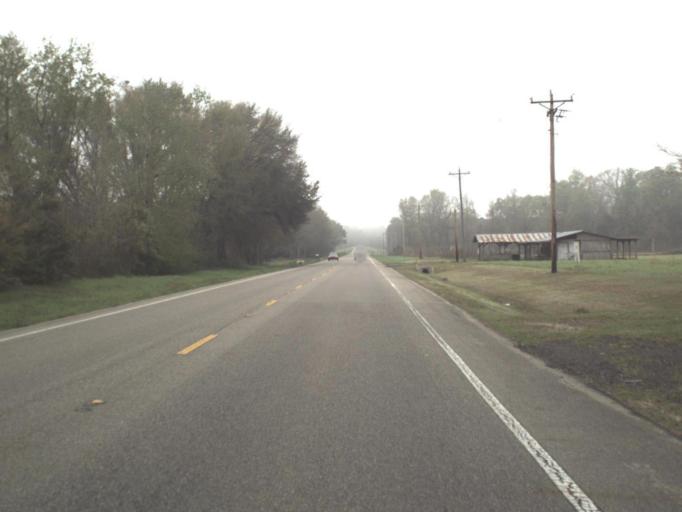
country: US
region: Florida
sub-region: Gadsden County
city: Gretna
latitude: 30.5784
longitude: -84.6729
